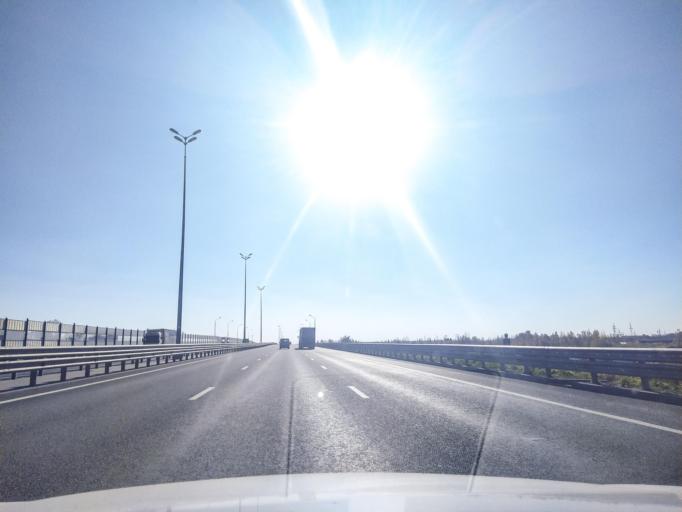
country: RU
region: Leningrad
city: Gatchina
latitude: 59.5549
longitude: 30.1655
